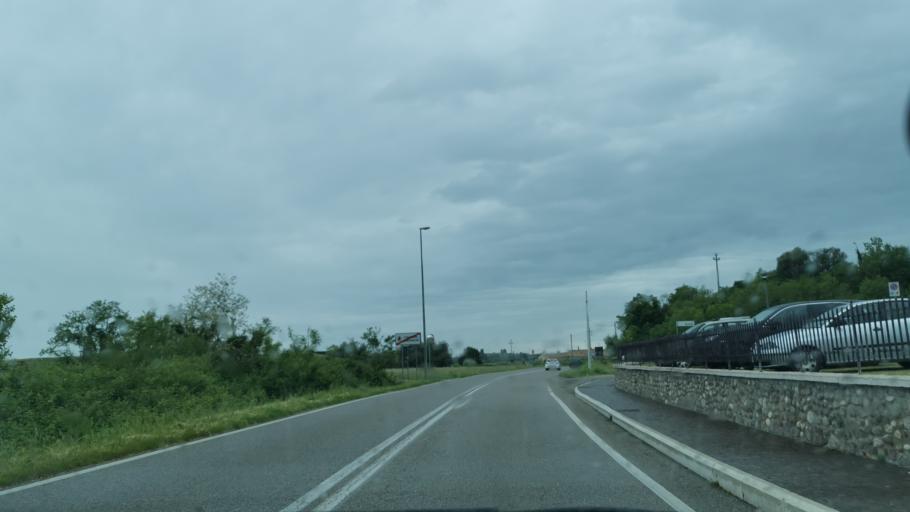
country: IT
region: Veneto
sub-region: Provincia di Verona
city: Cavajon Veronese
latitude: 45.5341
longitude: 10.7637
